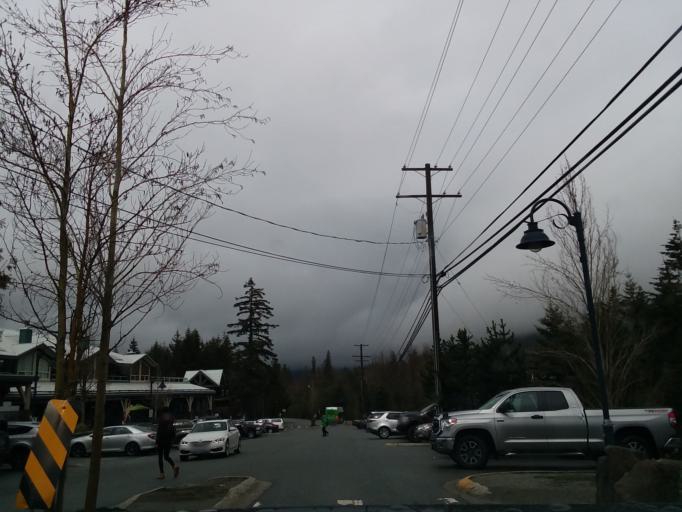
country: CA
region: British Columbia
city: Whistler
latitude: 50.1271
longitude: -122.9556
